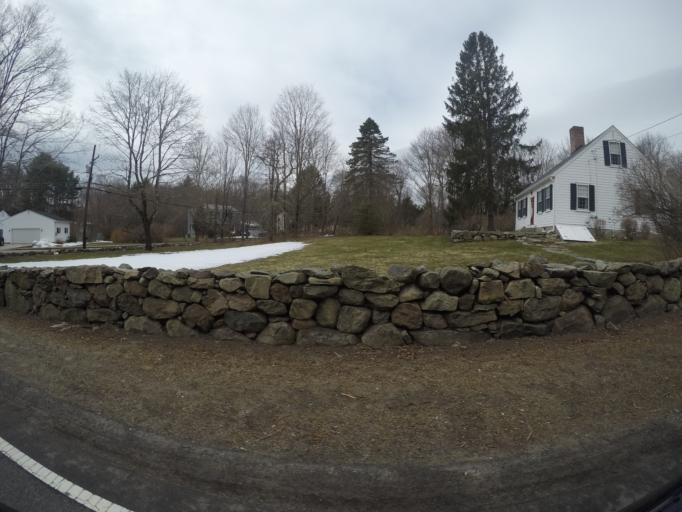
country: US
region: Massachusetts
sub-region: Bristol County
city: Easton
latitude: 42.0465
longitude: -71.1002
